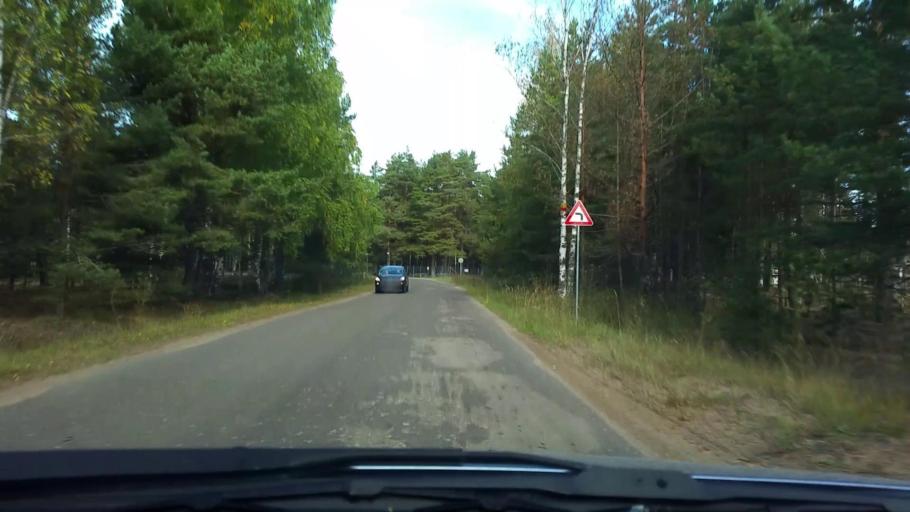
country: LV
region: Adazi
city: Adazi
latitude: 57.1218
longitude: 24.3601
